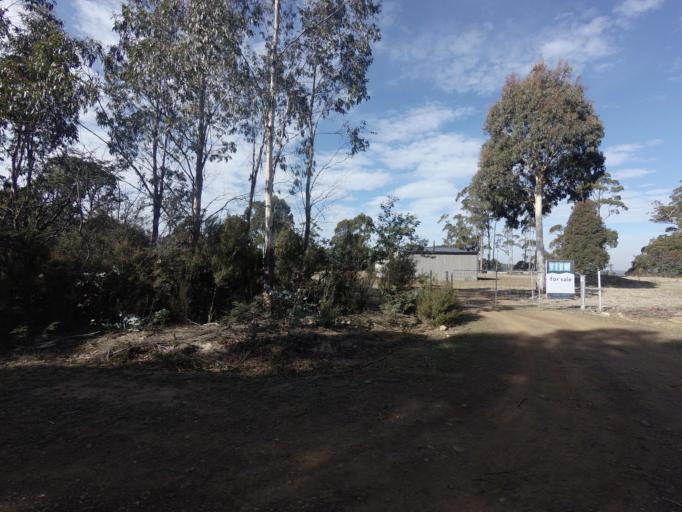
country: AU
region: Tasmania
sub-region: Sorell
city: Sorell
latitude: -42.5018
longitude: 147.4791
